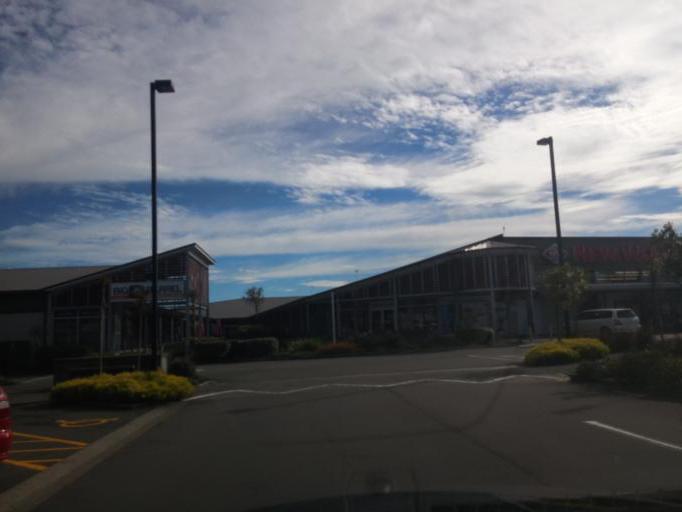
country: NZ
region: Manawatu-Wanganui
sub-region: Palmerston North City
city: Palmerston North
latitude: -40.3877
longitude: 175.6387
